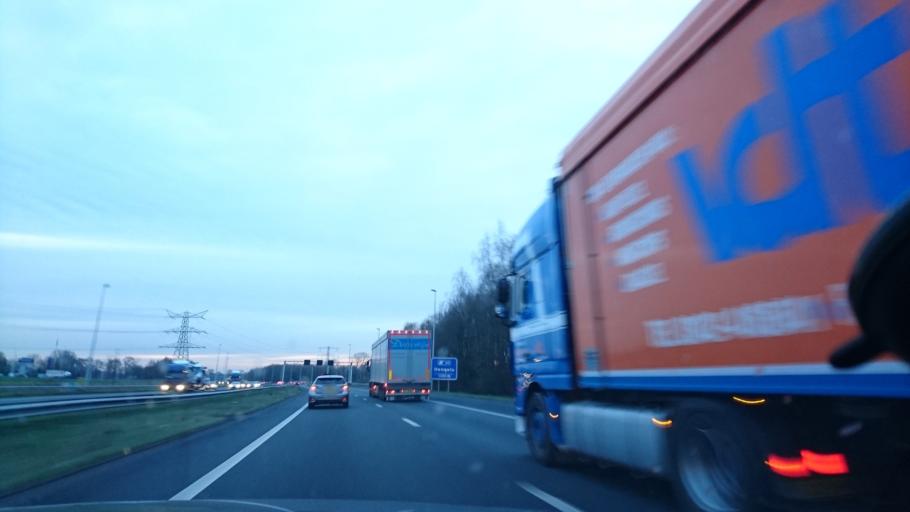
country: NL
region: Overijssel
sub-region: Gemeente Borne
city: Borne
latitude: 52.2852
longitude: 6.7443
